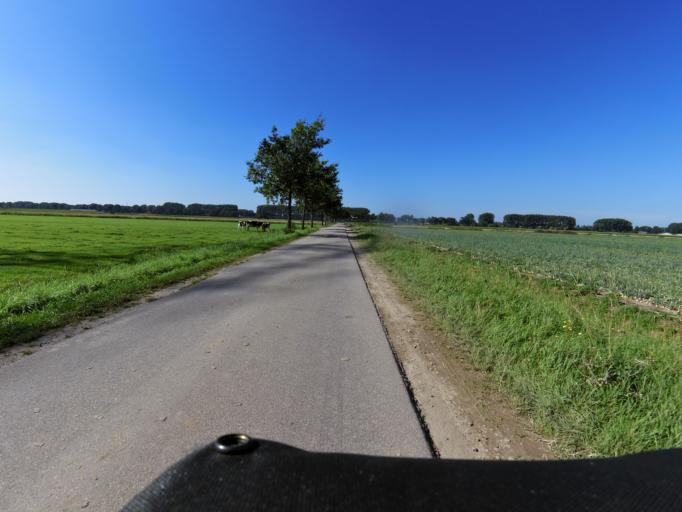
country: NL
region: South Holland
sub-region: Gemeente Dordrecht
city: Dordrecht
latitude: 51.7721
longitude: 4.7090
